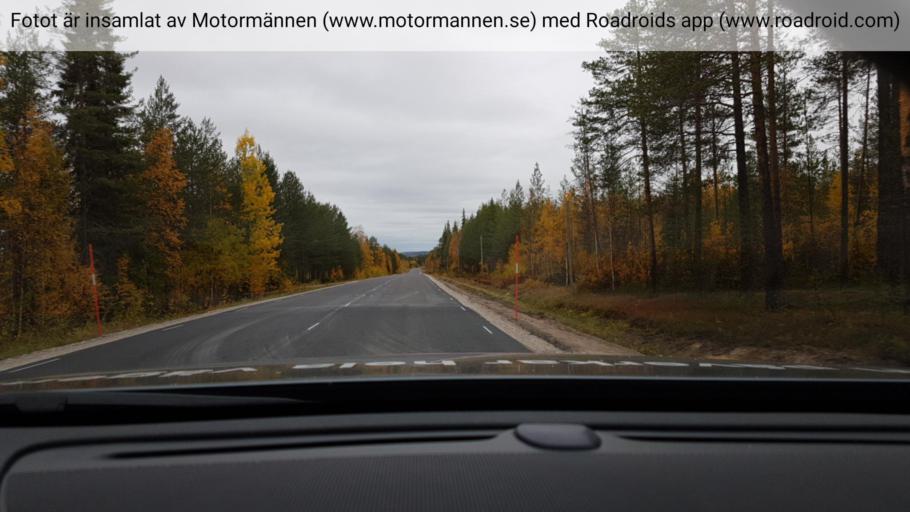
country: SE
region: Norrbotten
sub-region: Overkalix Kommun
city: OEverkalix
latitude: 66.3772
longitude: 22.8375
